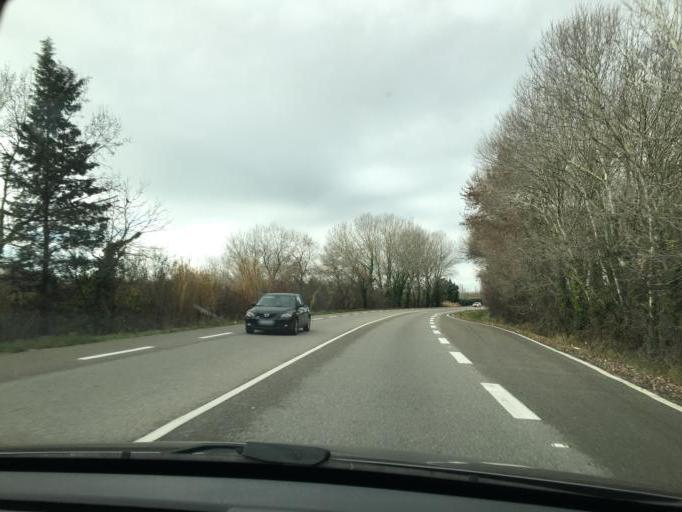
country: FR
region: Provence-Alpes-Cote d'Azur
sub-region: Departement du Vaucluse
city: Caumont-sur-Durance
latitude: 43.8816
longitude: 4.9604
